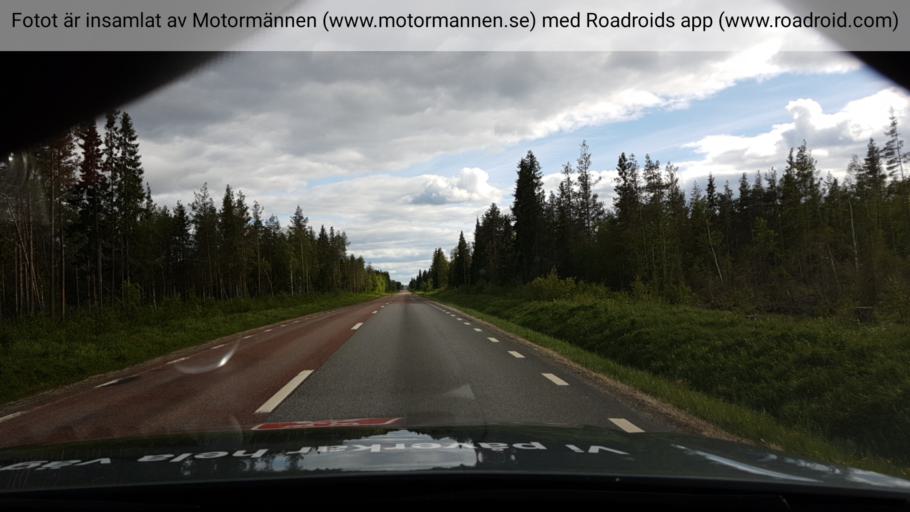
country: SE
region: Jaemtland
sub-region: Stroemsunds Kommun
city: Stroemsund
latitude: 63.7964
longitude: 15.5152
